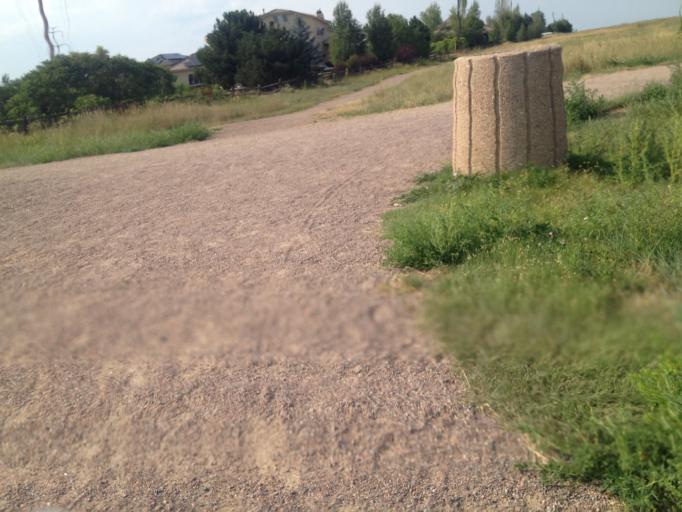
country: US
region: Colorado
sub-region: Boulder County
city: Superior
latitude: 39.9722
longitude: -105.1751
